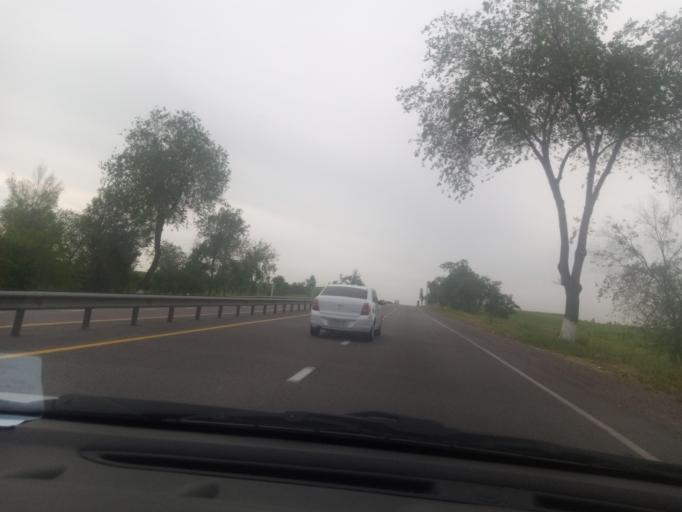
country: UZ
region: Toshkent
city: Tuytepa
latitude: 41.0659
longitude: 69.4803
